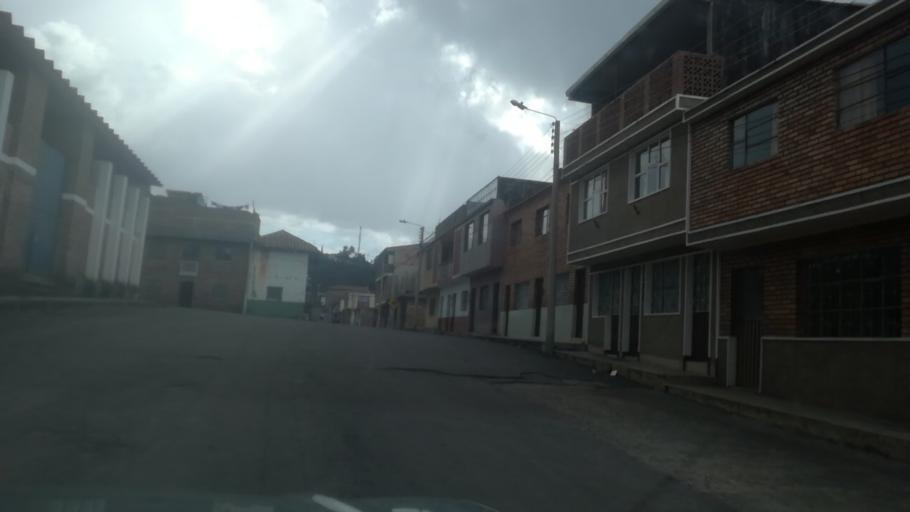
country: CO
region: Boyaca
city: Socha Viejo
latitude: 5.9992
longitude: -72.6904
